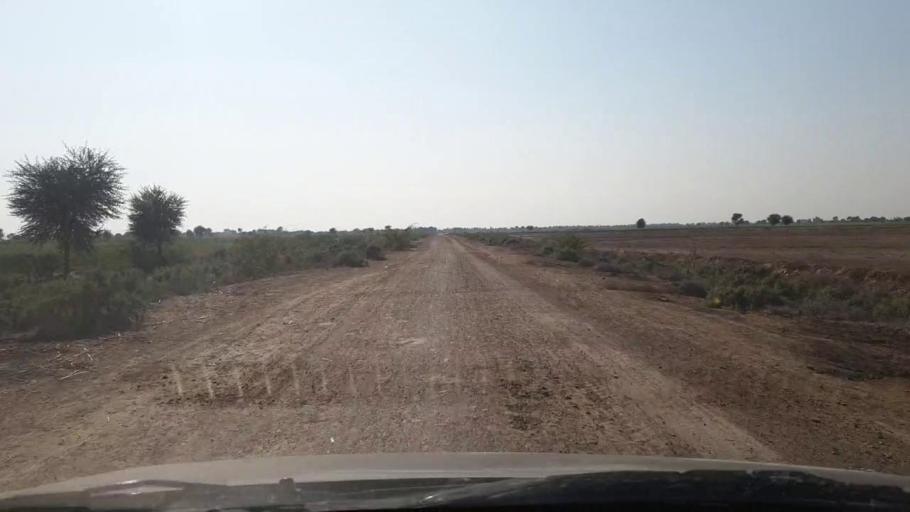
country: PK
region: Sindh
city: Digri
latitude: 25.1571
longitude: 69.2598
